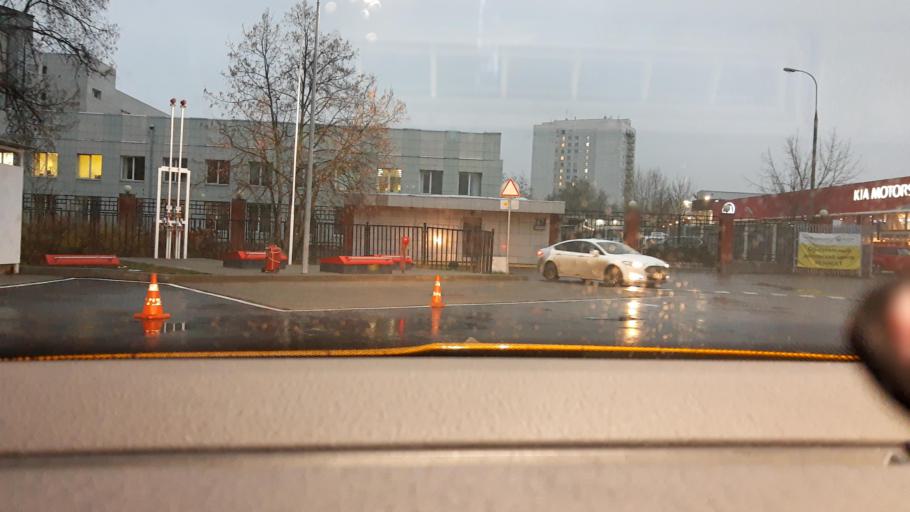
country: RU
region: Moskovskaya
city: Koptevo
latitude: 55.8313
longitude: 37.5177
